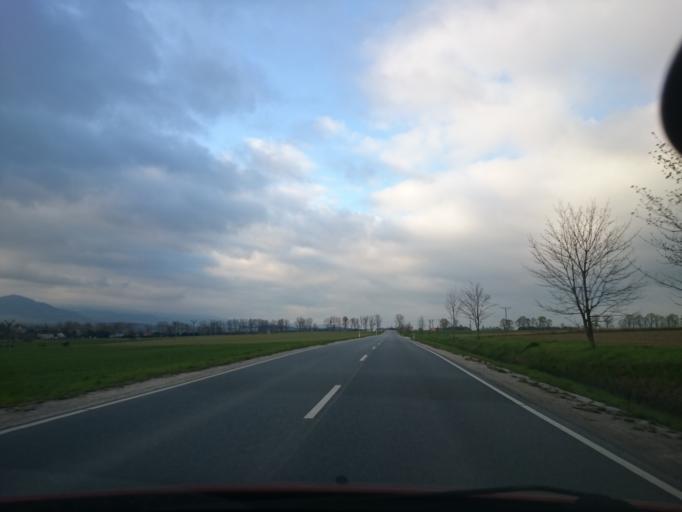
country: PL
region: Lower Silesian Voivodeship
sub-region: Powiat klodzki
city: Bystrzyca Klodzka
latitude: 50.2986
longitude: 16.6618
